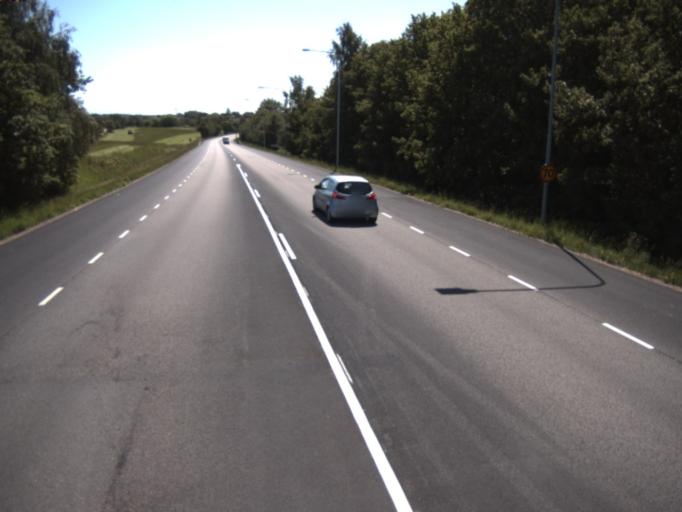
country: SE
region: Skane
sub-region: Helsingborg
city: Rydeback
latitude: 56.0084
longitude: 12.7627
